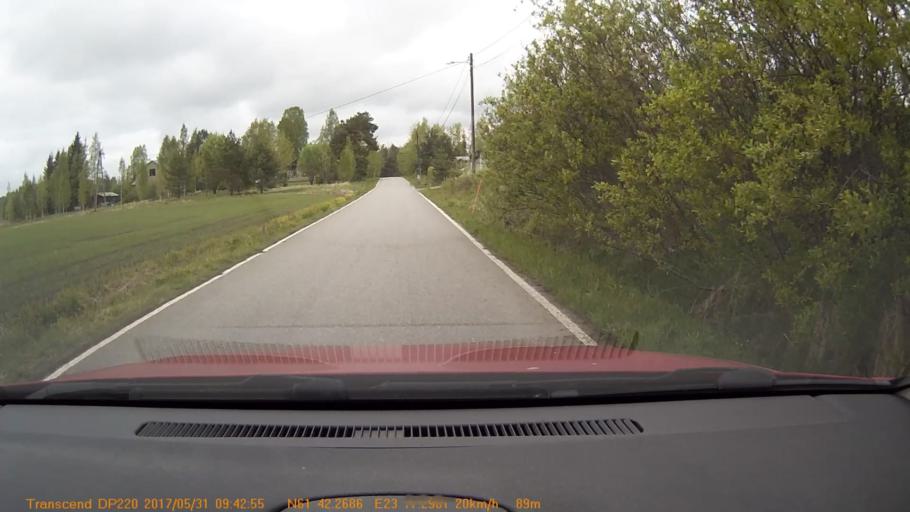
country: FI
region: Pirkanmaa
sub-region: Tampere
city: Viljakkala
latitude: 61.7044
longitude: 23.2883
